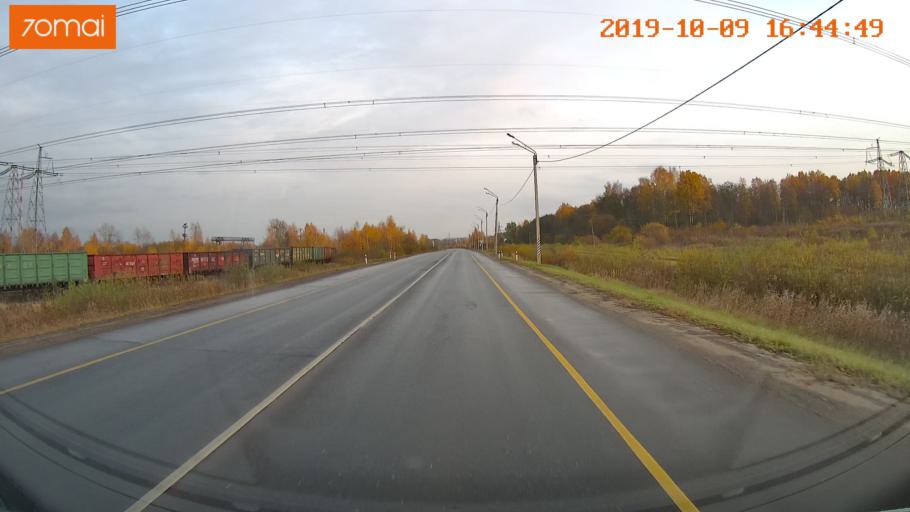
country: RU
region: Kostroma
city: Volgorechensk
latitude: 57.4499
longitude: 41.1461
